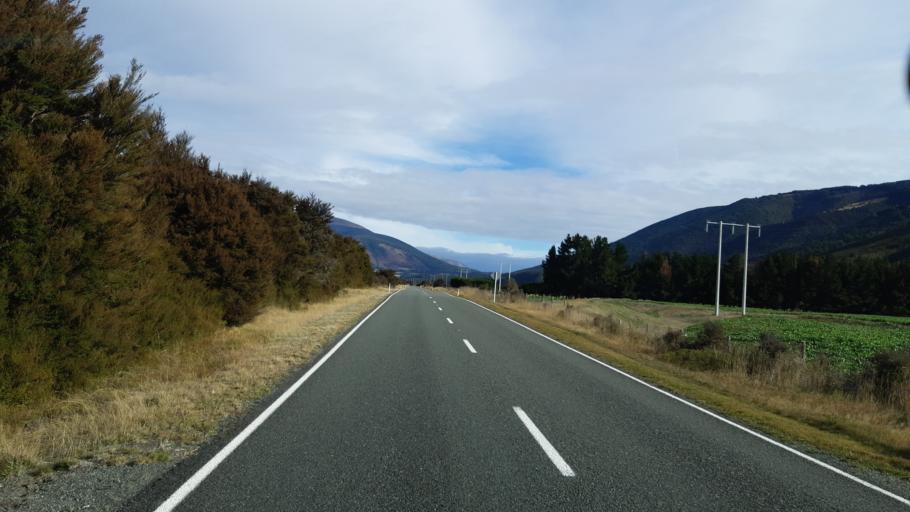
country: NZ
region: Tasman
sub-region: Tasman District
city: Wakefield
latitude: -41.7407
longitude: 173.0118
